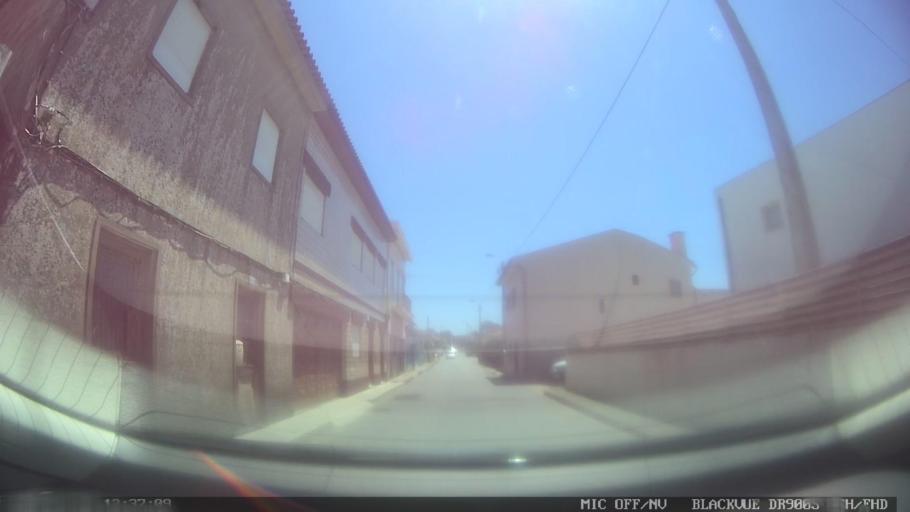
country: PT
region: Porto
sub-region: Matosinhos
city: Lavra
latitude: 41.2553
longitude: -8.7186
